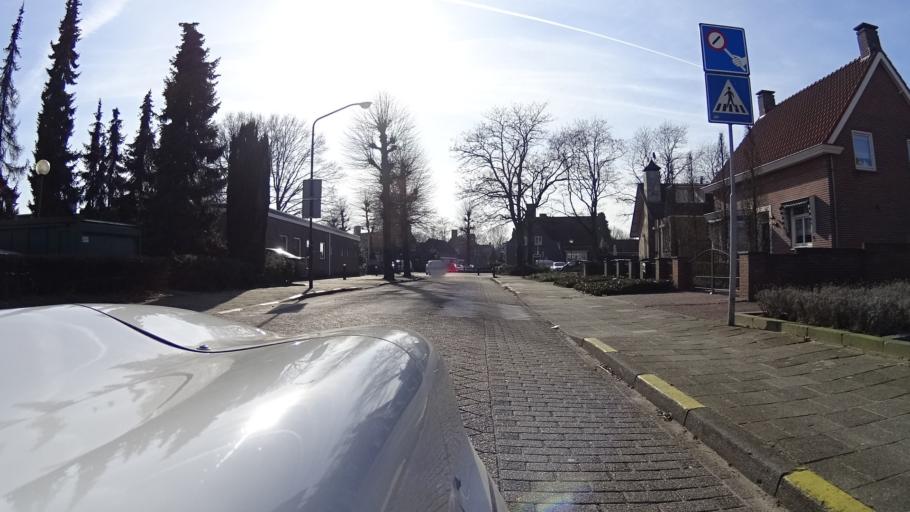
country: NL
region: North Brabant
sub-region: Gemeente Veghel
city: Erp
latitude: 51.5991
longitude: 5.6110
